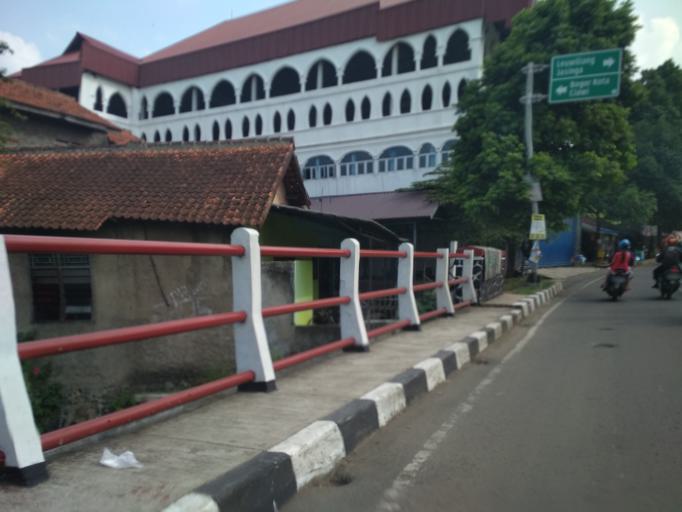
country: ID
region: West Java
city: Bogor
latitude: -6.5719
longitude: 106.7505
